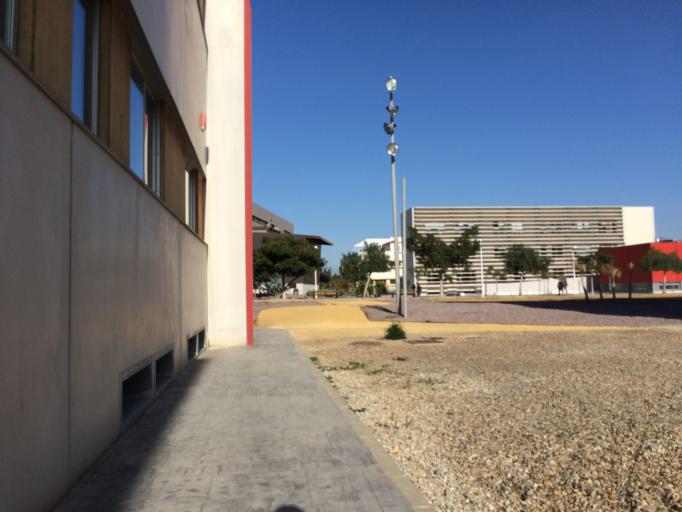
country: ES
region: Andalusia
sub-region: Provincia de Almeria
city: Almeria
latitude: 36.8292
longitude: -2.4075
